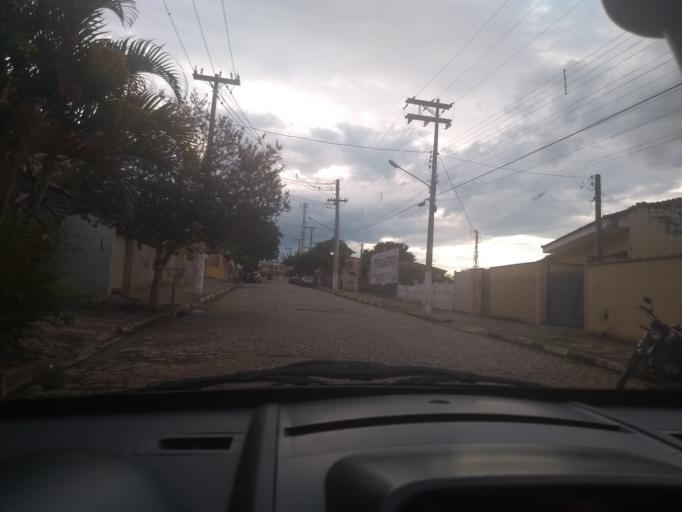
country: BR
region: Sao Paulo
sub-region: Casa Branca
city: Casa Branca
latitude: -21.7745
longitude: -47.0782
